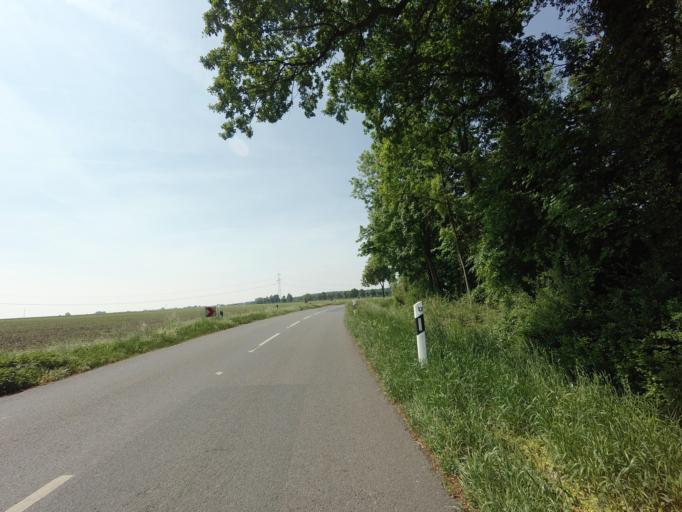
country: DE
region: Lower Saxony
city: Adenbuettel
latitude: 52.3718
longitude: 10.4365
